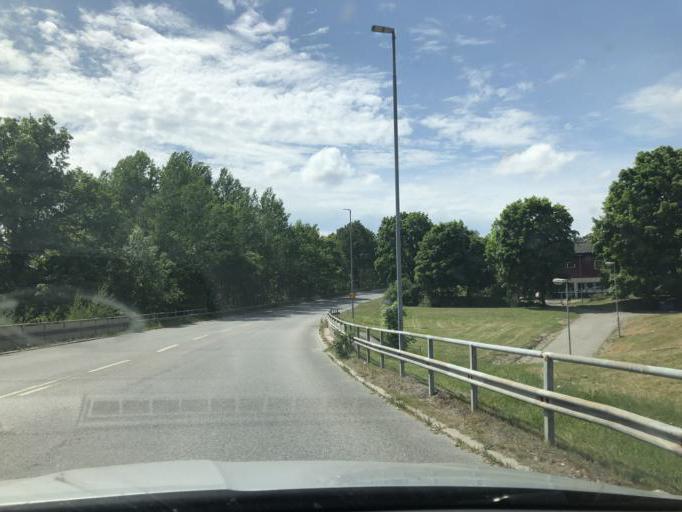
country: SE
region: Stockholm
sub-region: Botkyrka Kommun
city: Alby
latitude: 59.2412
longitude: 17.8544
